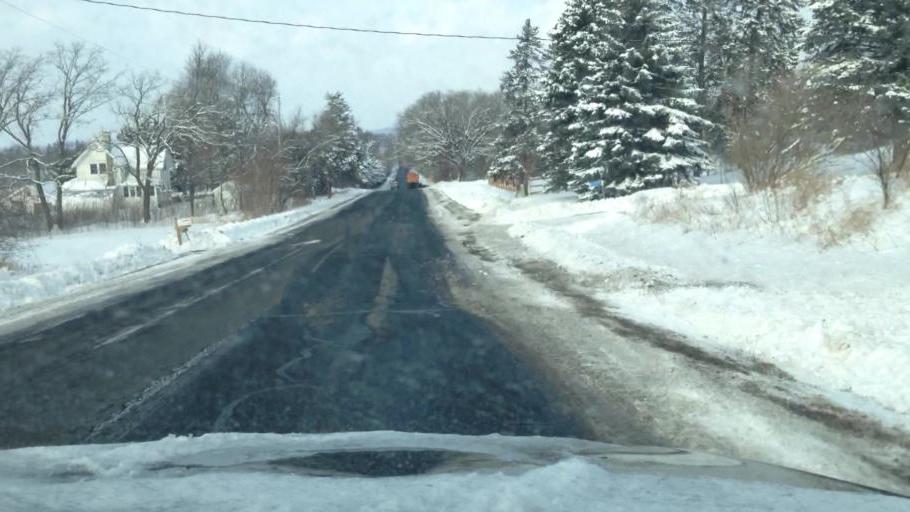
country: US
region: Wisconsin
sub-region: Walworth County
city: East Troy
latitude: 42.7588
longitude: -88.4457
